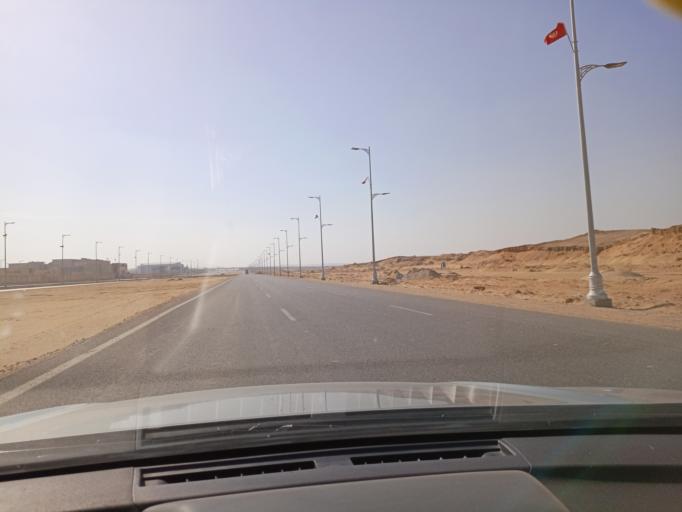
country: EG
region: Muhafazat al Qalyubiyah
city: Al Khankah
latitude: 30.0444
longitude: 31.7043
